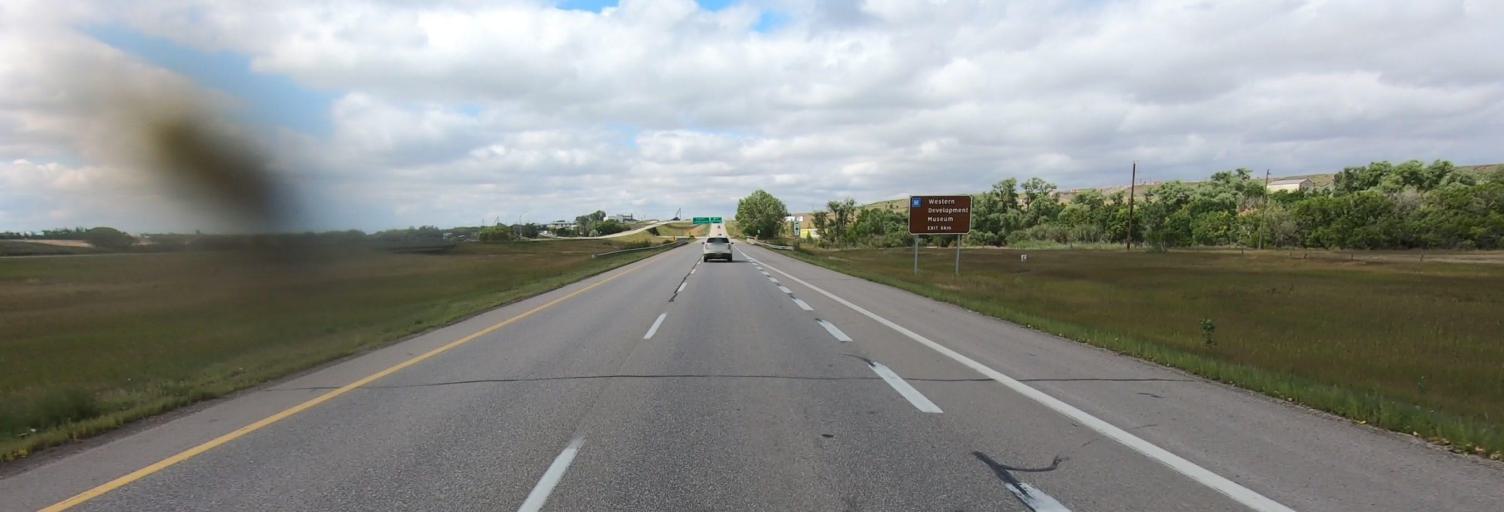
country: CA
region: Saskatchewan
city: Moose Jaw
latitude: 50.3947
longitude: -105.4737
